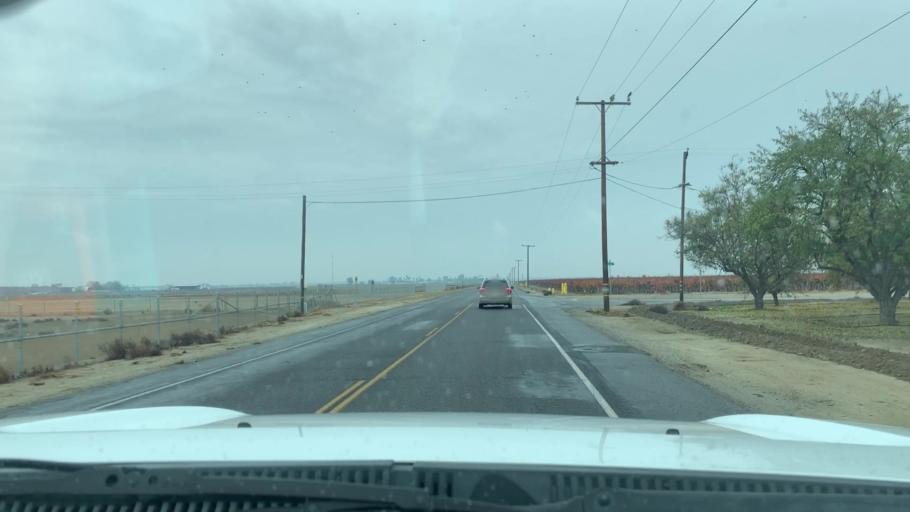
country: US
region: California
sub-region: Kern County
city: Delano
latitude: 35.7613
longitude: -119.3125
